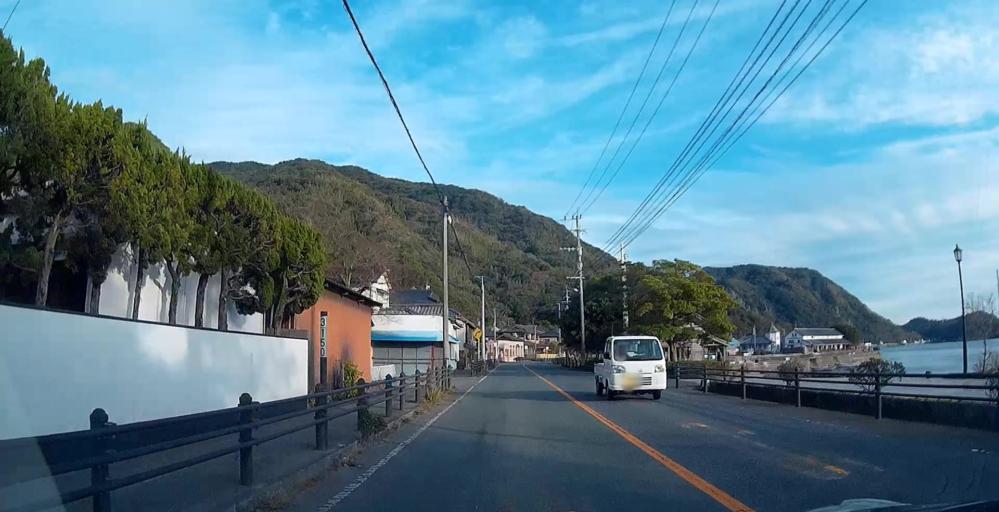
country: JP
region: Nagasaki
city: Shimabara
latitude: 32.6235
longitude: 130.4541
